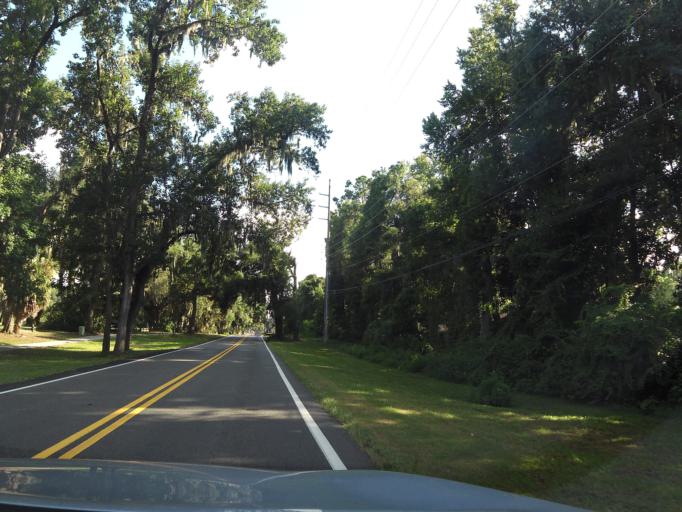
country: US
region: Georgia
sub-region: Glynn County
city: Saint Simon Mills
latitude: 31.1924
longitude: -81.3765
